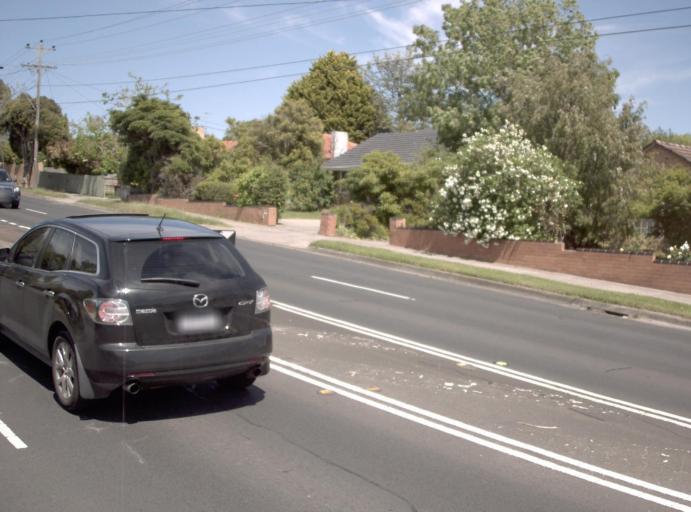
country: AU
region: Victoria
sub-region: Monash
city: Notting Hill
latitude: -37.8852
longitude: 145.1460
